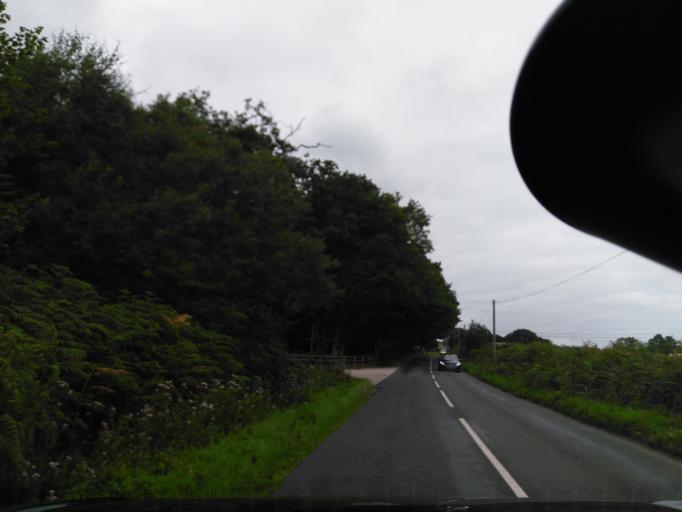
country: GB
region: England
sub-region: Dorset
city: Lytchett Matravers
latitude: 50.7416
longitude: -2.1236
